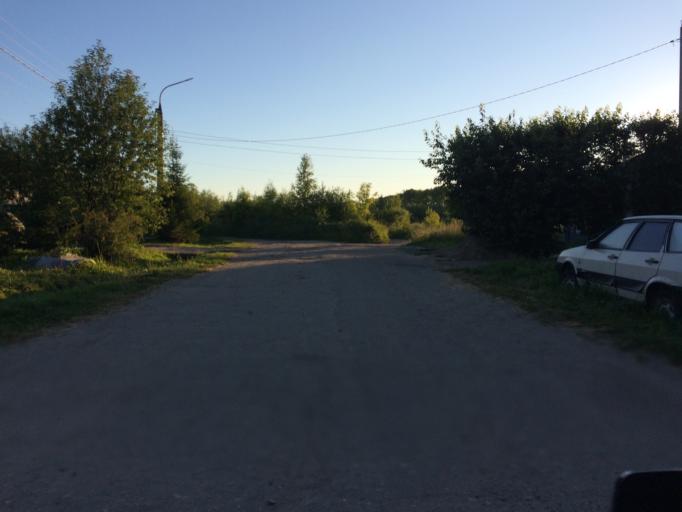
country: RU
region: Mariy-El
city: Yoshkar-Ola
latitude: 56.6547
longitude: 47.8978
